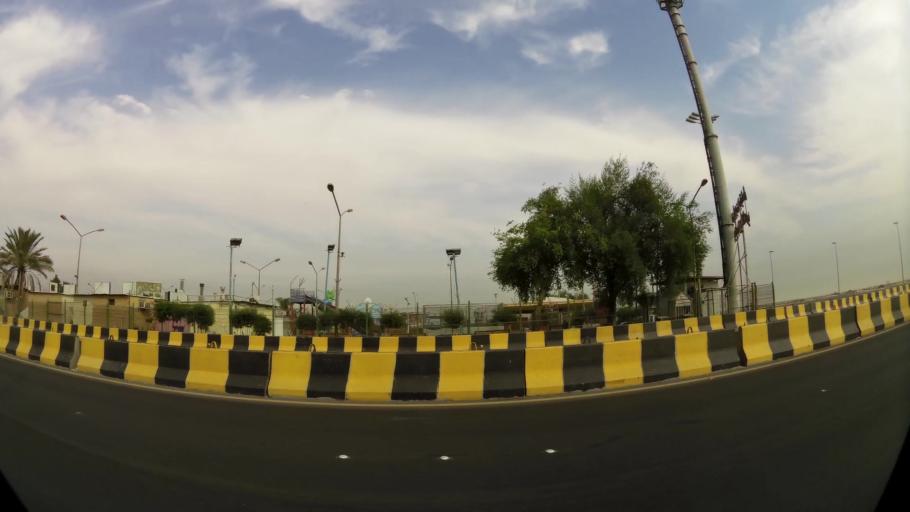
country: KW
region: Al Asimah
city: Ar Rabiyah
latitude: 29.3184
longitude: 47.8603
